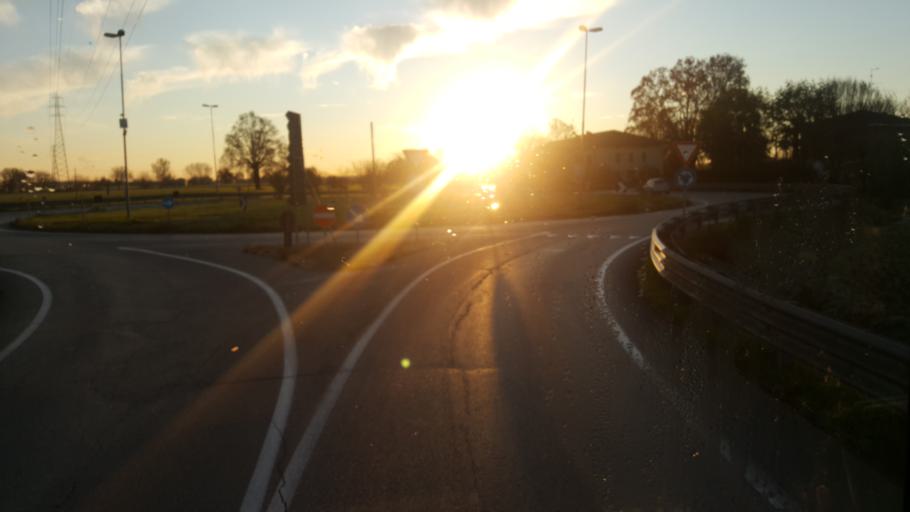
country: IT
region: Emilia-Romagna
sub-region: Provincia di Parma
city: Fontanellato
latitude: 44.8698
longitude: 10.1949
